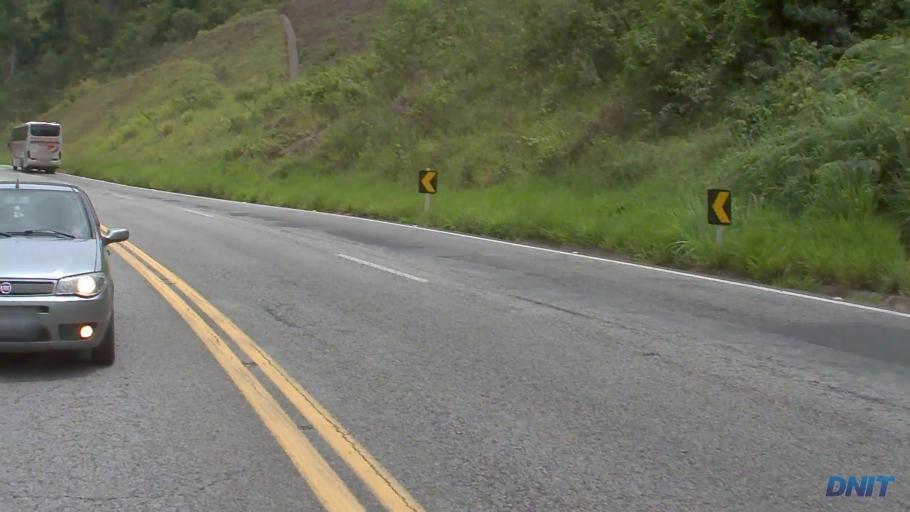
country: BR
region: Minas Gerais
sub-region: Nova Era
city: Nova Era
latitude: -19.6417
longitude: -42.9034
